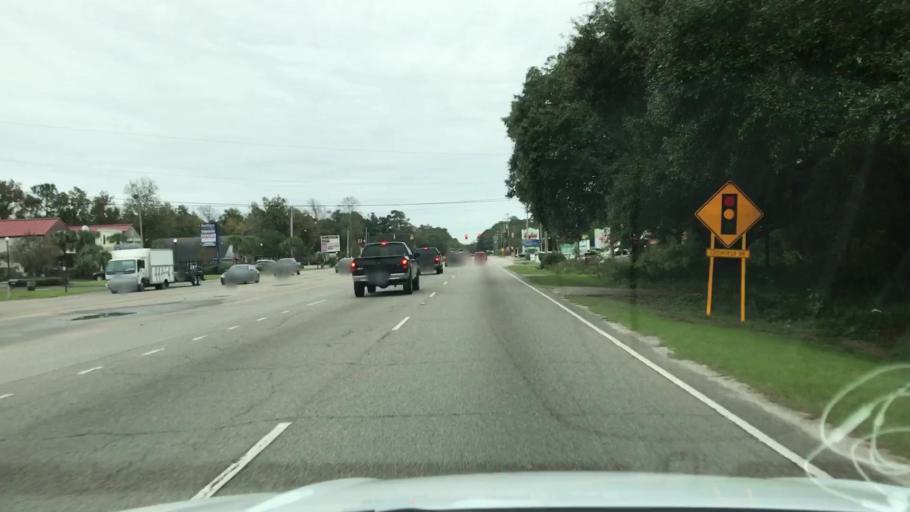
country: US
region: South Carolina
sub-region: Georgetown County
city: Murrells Inlet
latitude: 33.4700
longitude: -79.1059
